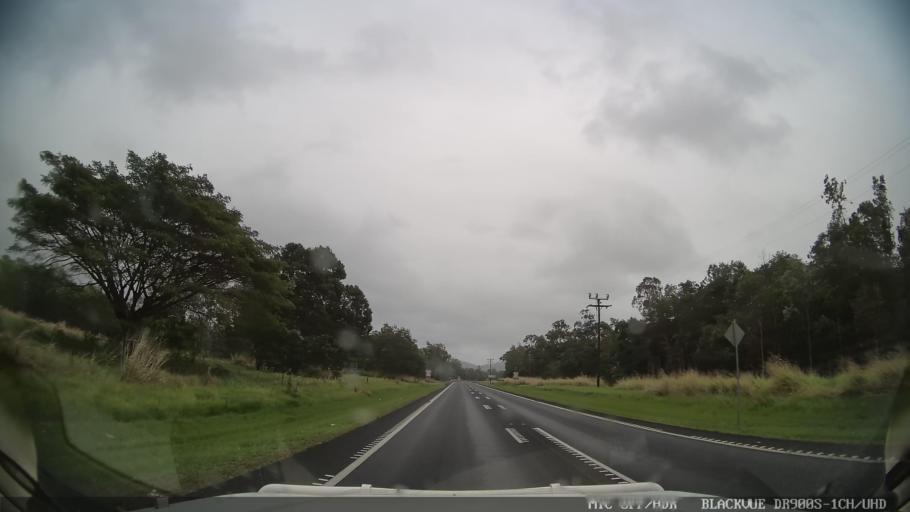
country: AU
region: Queensland
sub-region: Hinchinbrook
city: Ingham
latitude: -18.2044
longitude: 145.9553
